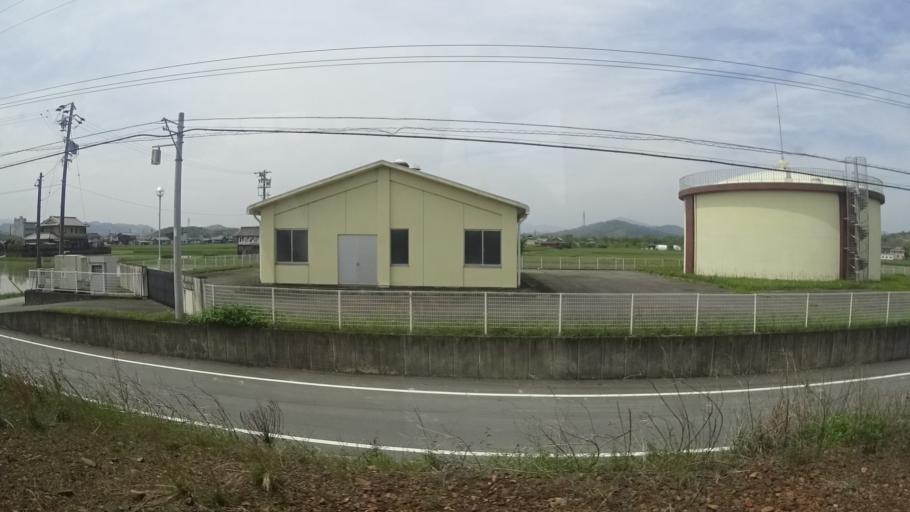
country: JP
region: Mie
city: Ise
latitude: 34.5182
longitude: 136.5722
